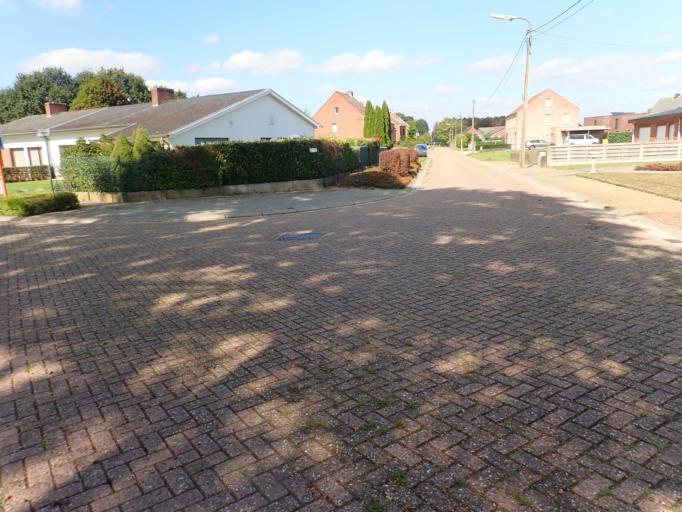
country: BE
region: Flanders
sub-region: Provincie Antwerpen
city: Westerlo
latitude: 51.1243
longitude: 4.9065
